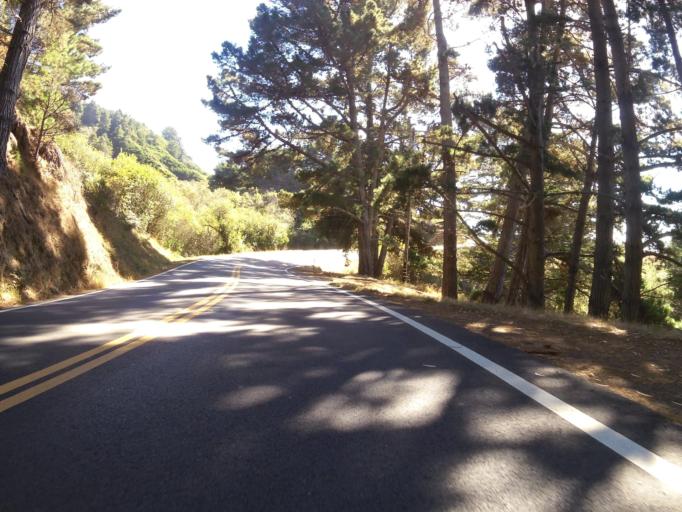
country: US
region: California
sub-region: Mendocino County
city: Fort Bragg
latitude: 39.6269
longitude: -123.7825
